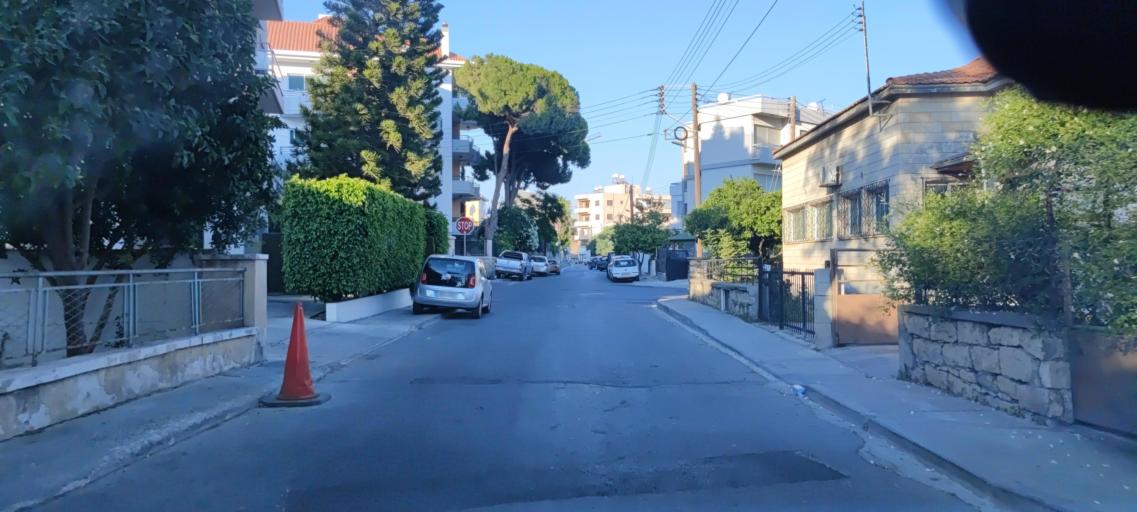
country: CY
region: Limassol
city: Limassol
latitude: 34.6763
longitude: 33.0360
